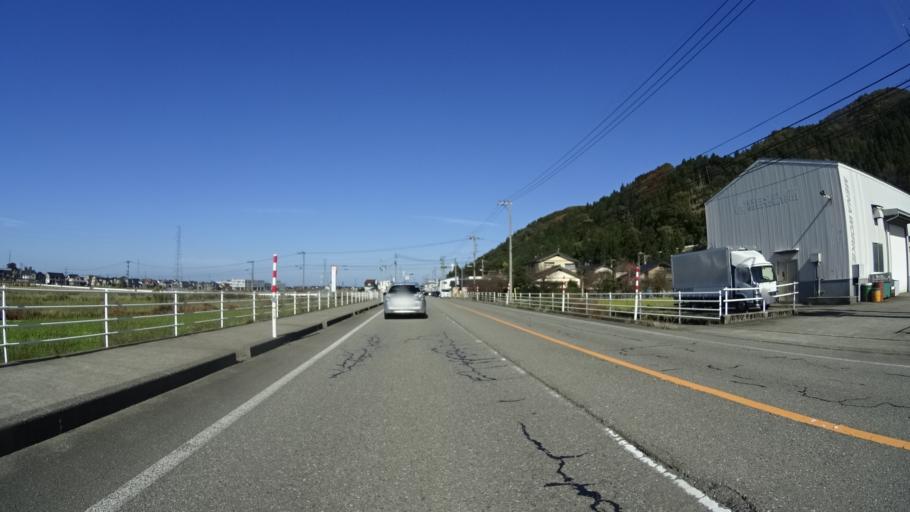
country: JP
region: Ishikawa
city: Tsurugi-asahimachi
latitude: 36.4641
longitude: 136.6201
